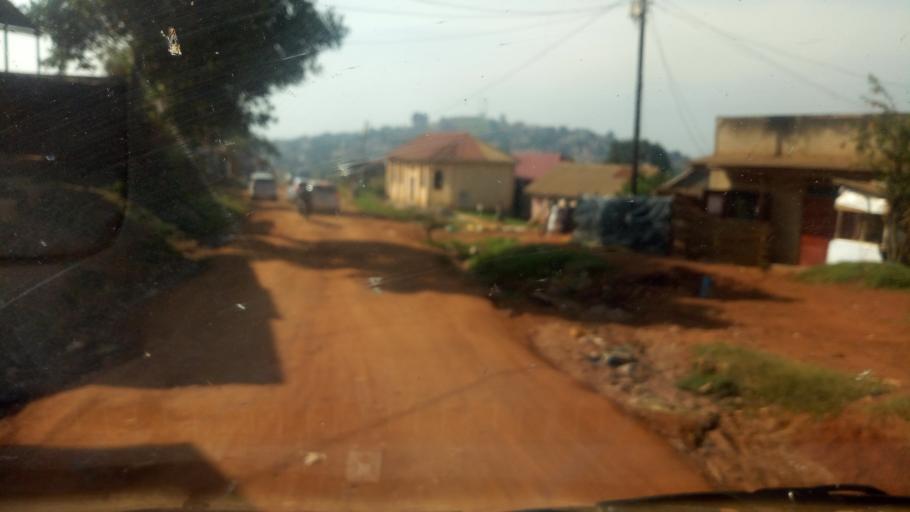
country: UG
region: Central Region
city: Kampala Central Division
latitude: 0.3798
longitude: 32.5470
